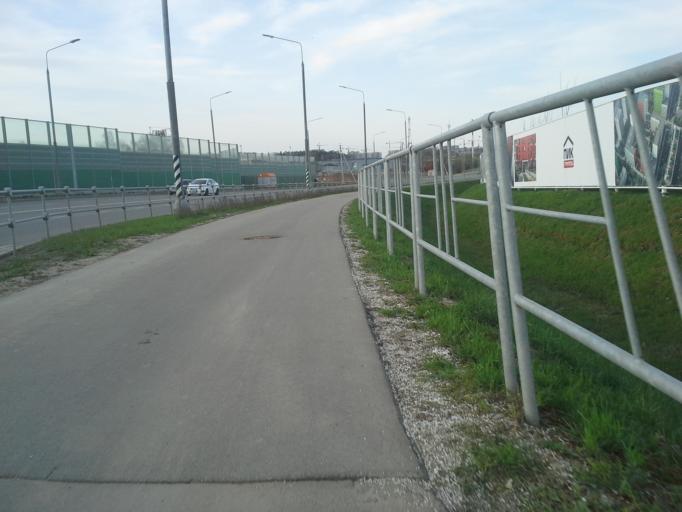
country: RU
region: Moskovskaya
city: Kommunarka
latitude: 55.5498
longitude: 37.4861
